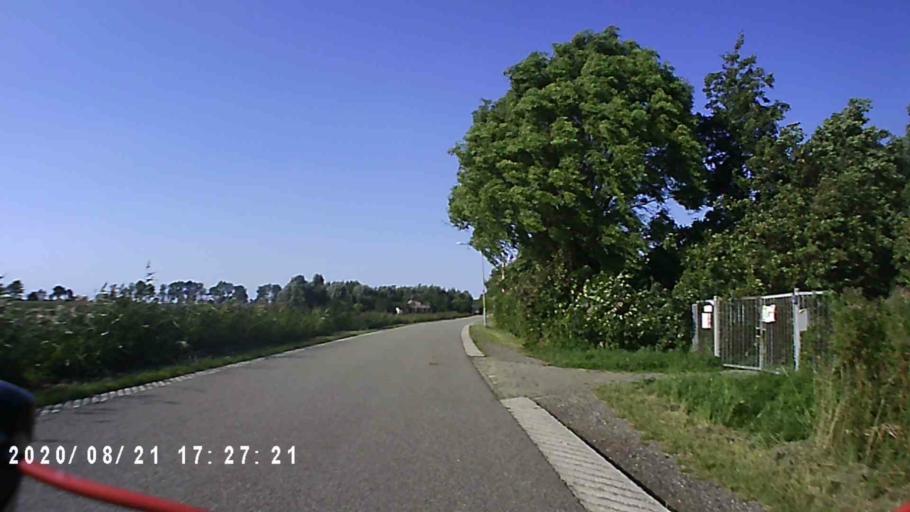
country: NL
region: Groningen
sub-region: Gemeente Bedum
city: Bedum
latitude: 53.2653
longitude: 6.5894
